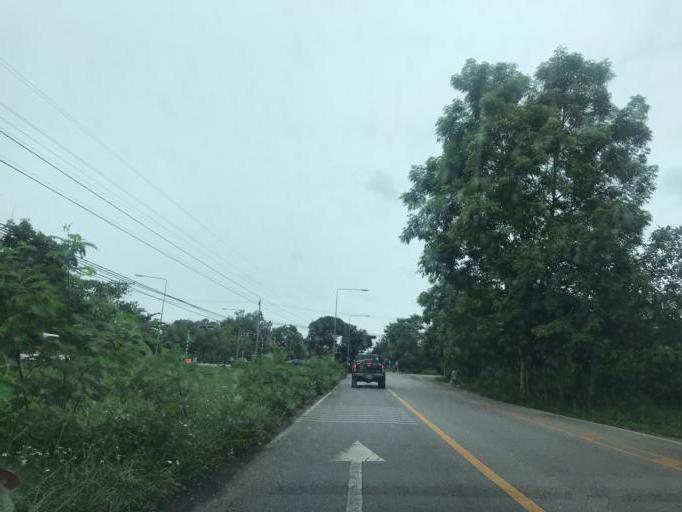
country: TH
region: Chiang Mai
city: Saraphi
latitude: 18.7173
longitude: 99.0387
